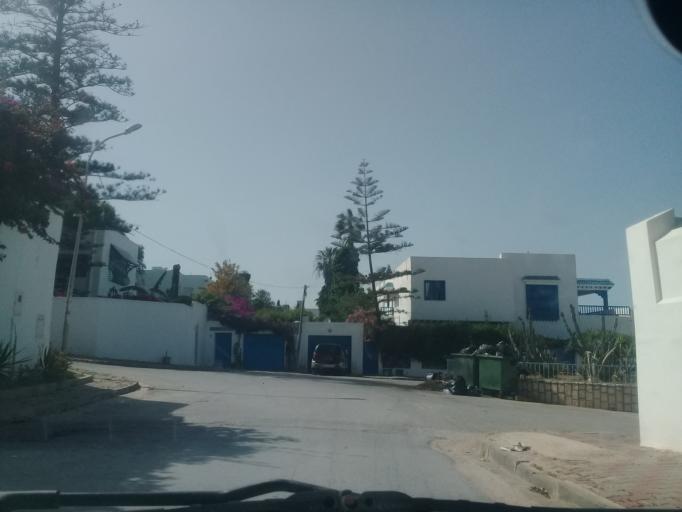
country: TN
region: Tunis
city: Al Marsa
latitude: 36.8888
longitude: 10.3261
